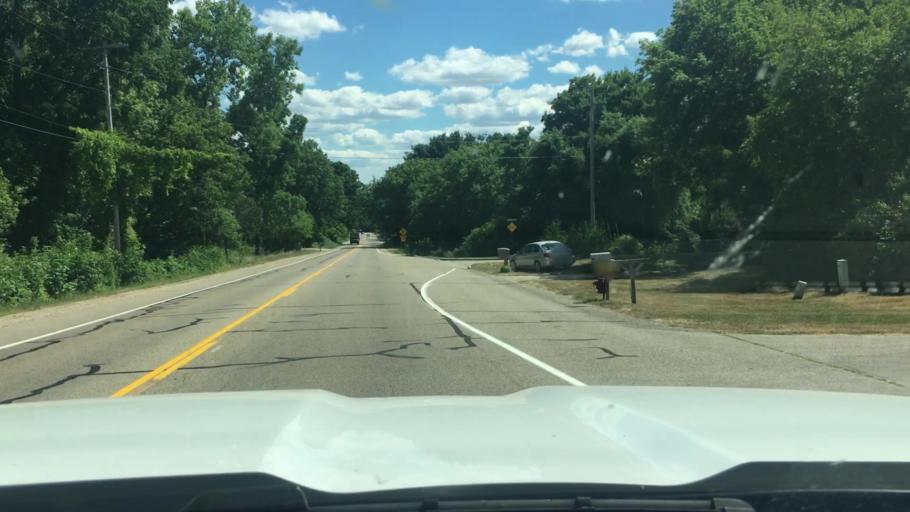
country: US
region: Michigan
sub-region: Kent County
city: Comstock Park
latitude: 43.0604
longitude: -85.6539
